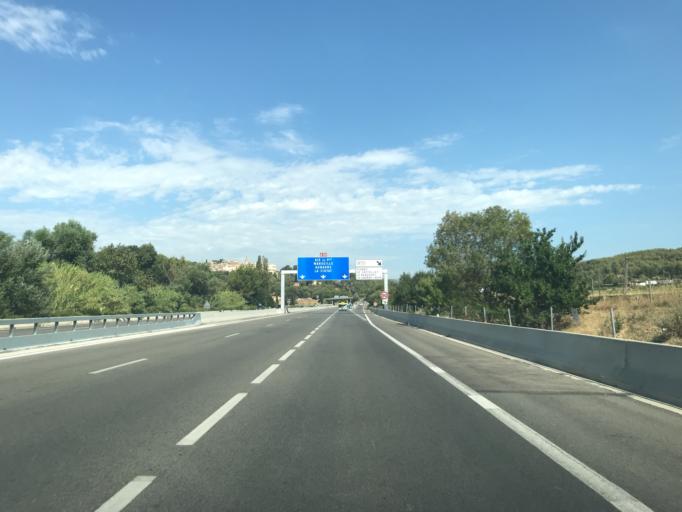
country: FR
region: Provence-Alpes-Cote d'Azur
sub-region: Departement du Var
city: Le Castellet
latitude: 43.1881
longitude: 5.7674
